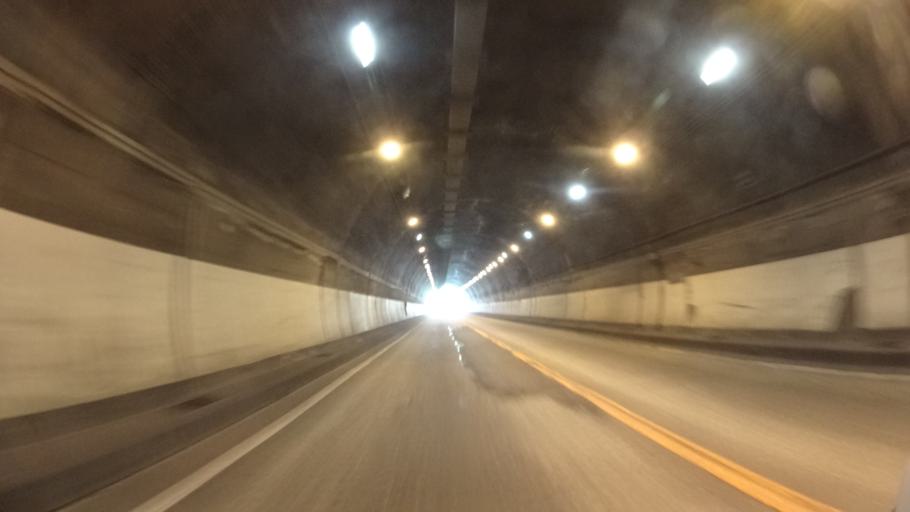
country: JP
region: Tottori
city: Tottori
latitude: 35.5230
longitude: 134.0909
